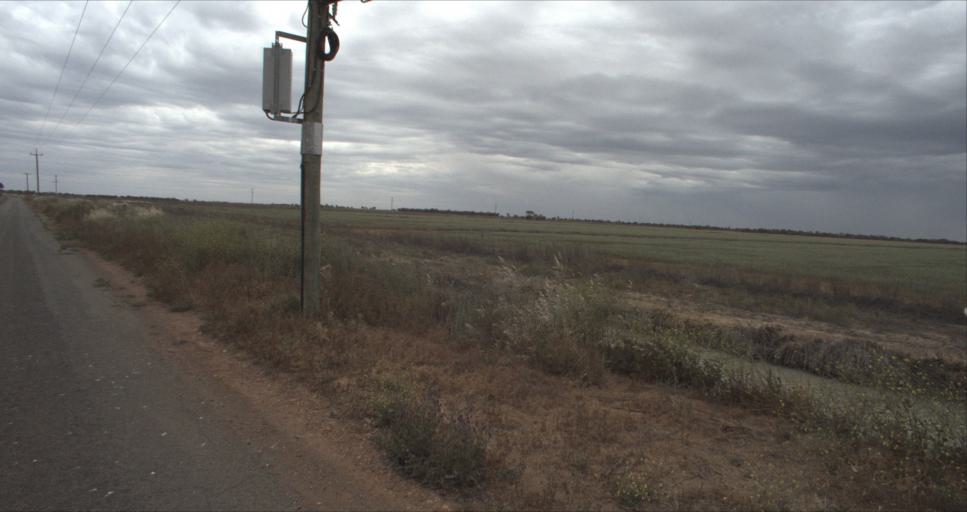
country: AU
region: New South Wales
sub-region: Leeton
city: Leeton
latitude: -34.4322
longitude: 146.3364
